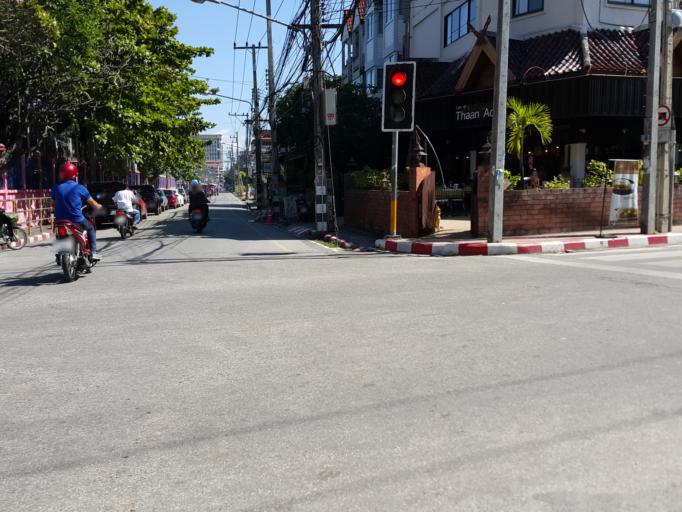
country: TH
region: Chiang Mai
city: Chiang Mai
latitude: 18.7856
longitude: 98.9883
